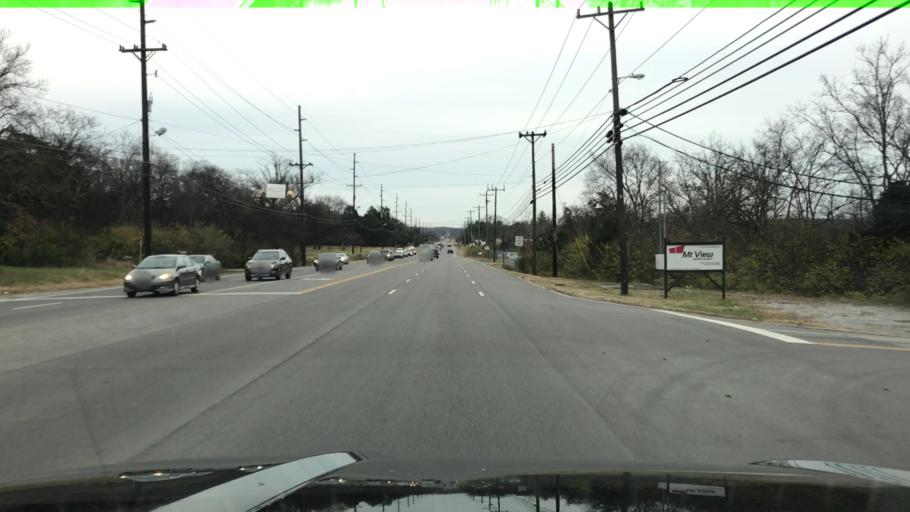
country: US
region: Tennessee
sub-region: Rutherford County
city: La Vergne
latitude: 36.0393
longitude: -86.6030
